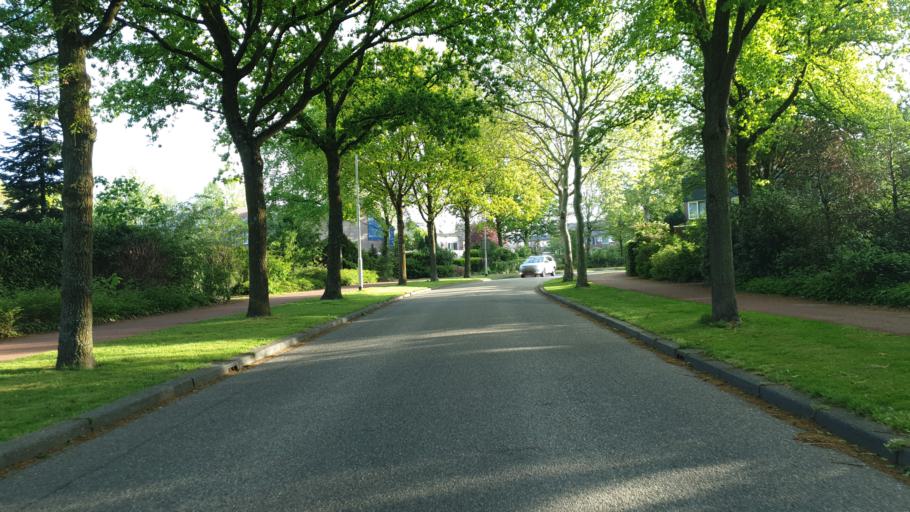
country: NL
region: North Brabant
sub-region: Gemeente Cuijk
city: Cuijk
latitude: 51.7799
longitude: 5.8576
